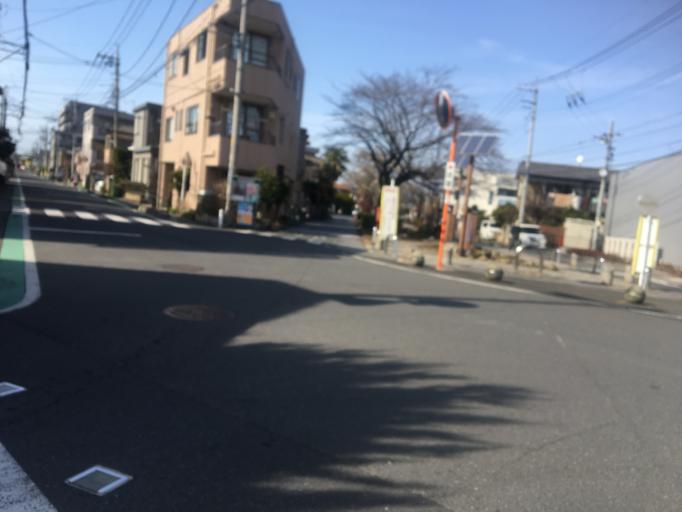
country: JP
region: Saitama
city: Shiki
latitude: 35.8356
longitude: 139.5883
